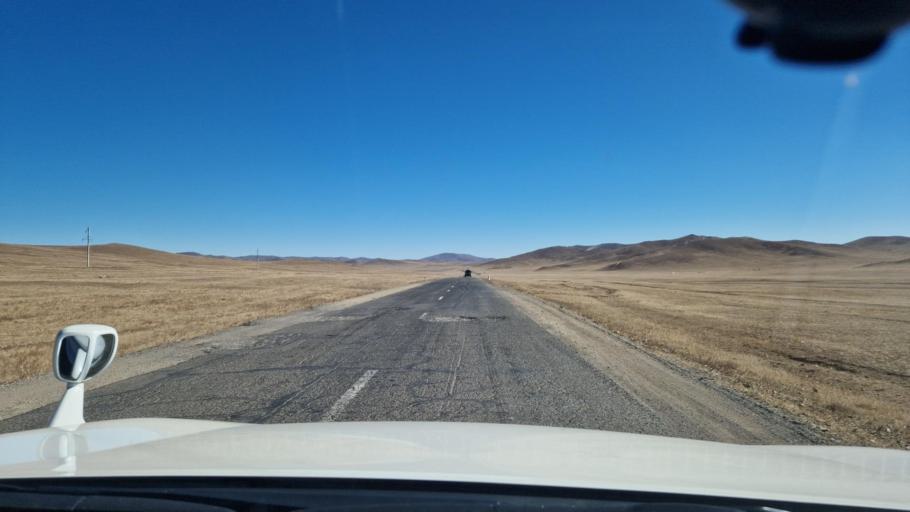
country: MN
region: Hentiy
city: Modot
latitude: 47.7677
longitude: 108.8834
